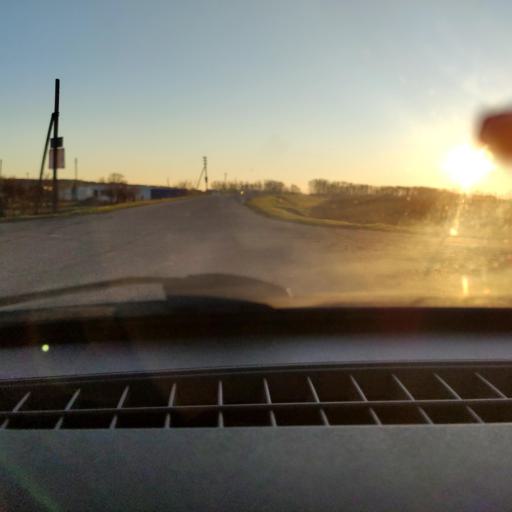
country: RU
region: Bashkortostan
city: Avdon
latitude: 54.5493
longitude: 55.6576
